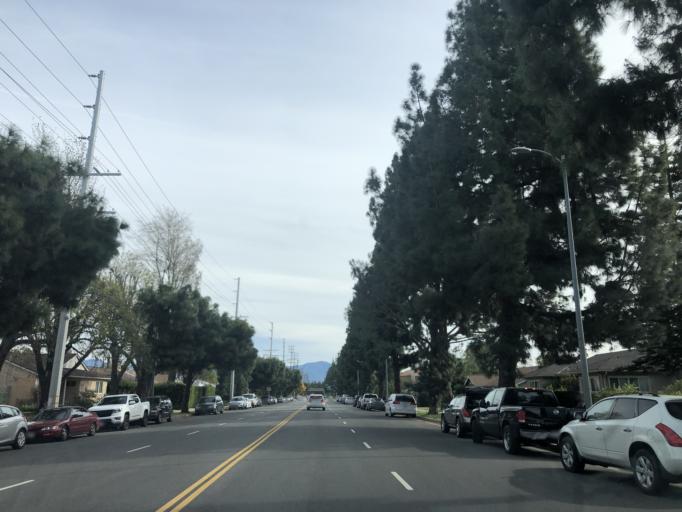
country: US
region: California
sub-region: Los Angeles County
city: San Fernando
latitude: 34.2719
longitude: -118.4789
